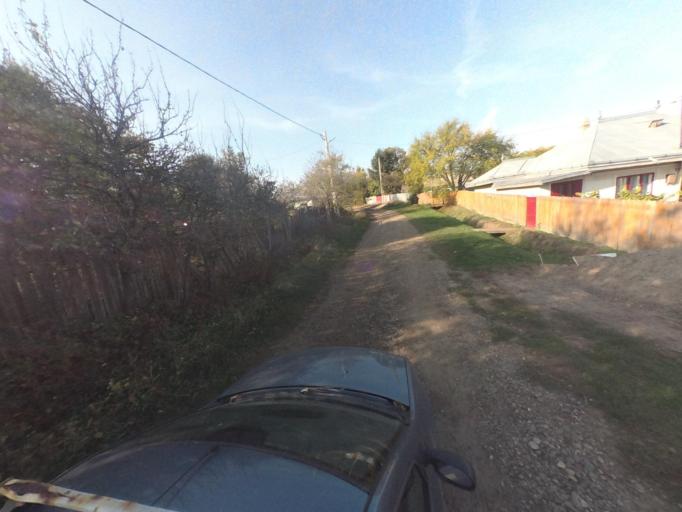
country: RO
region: Vaslui
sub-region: Comuna Bacesti
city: Bacesti
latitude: 46.8751
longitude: 27.1957
